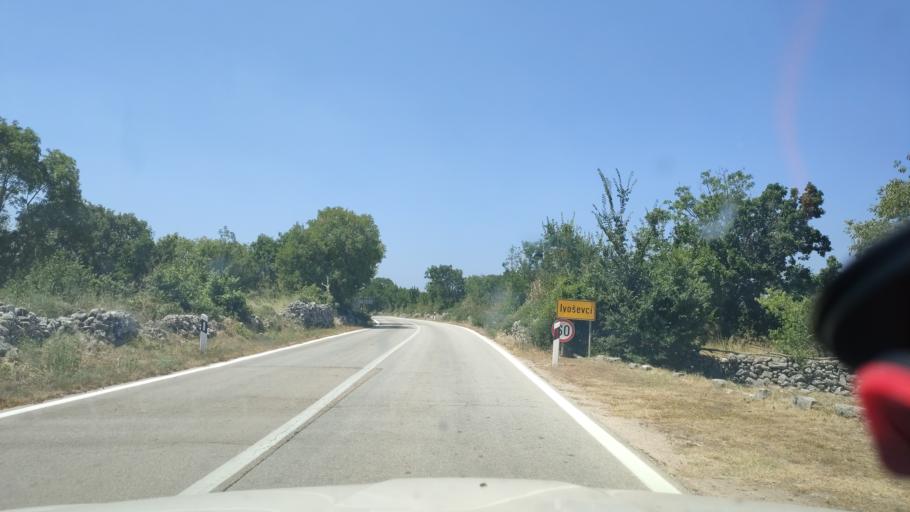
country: HR
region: Sibensko-Kniniska
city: Kistanje
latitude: 44.0167
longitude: 16.0148
